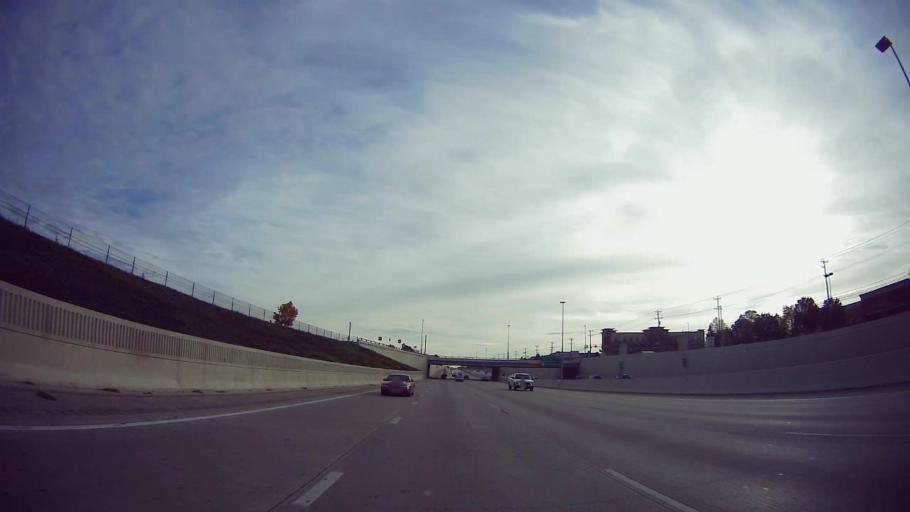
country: US
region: Michigan
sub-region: Wayne County
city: Livonia
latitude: 42.3839
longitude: -83.3284
